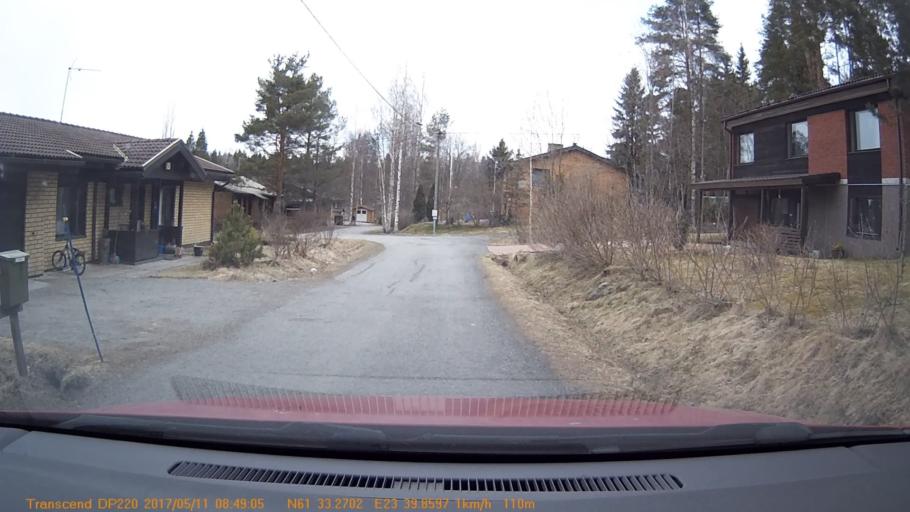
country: FI
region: Pirkanmaa
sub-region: Tampere
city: Yloejaervi
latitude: 61.5545
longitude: 23.6643
